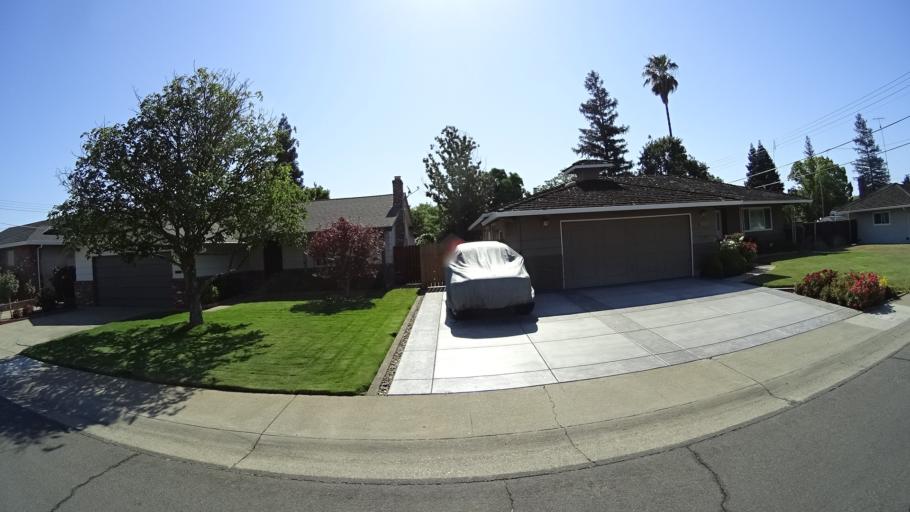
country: US
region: California
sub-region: Sacramento County
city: Florin
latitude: 38.5386
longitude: -121.4224
